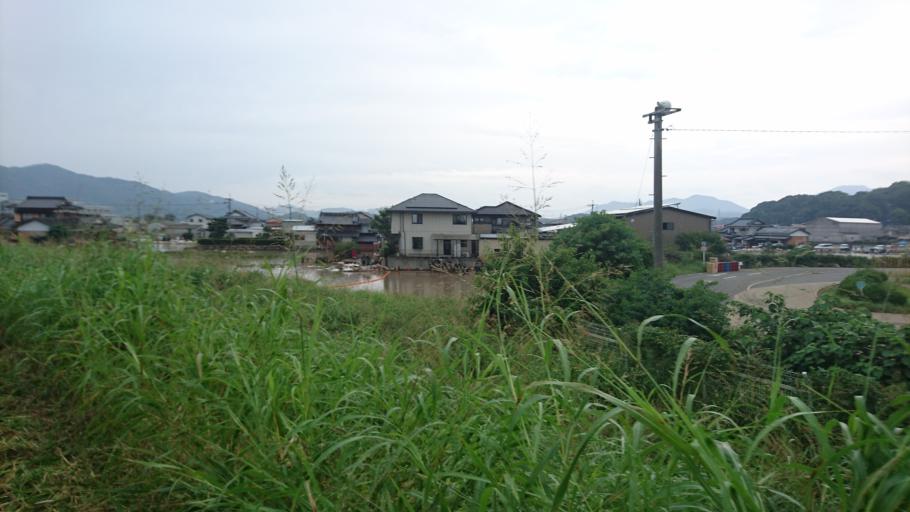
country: JP
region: Saga Prefecture
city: Takeocho-takeo
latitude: 33.2098
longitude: 130.1070
